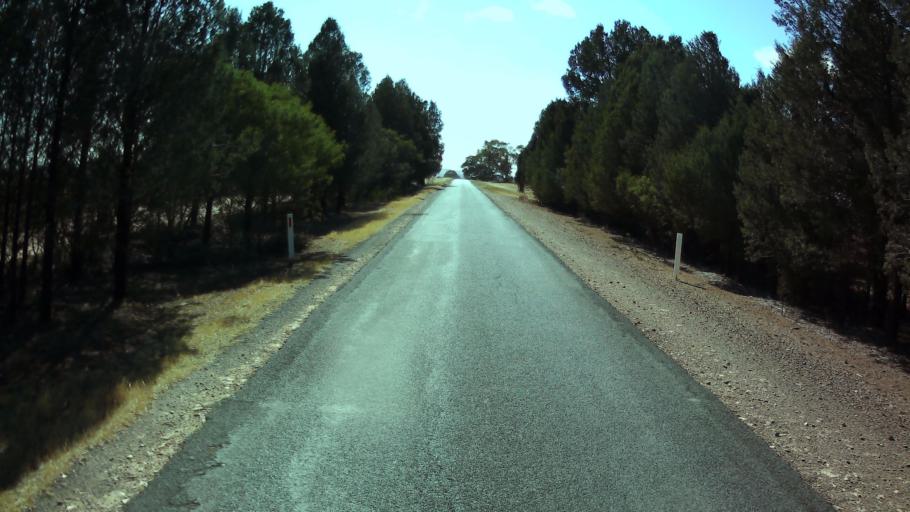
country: AU
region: New South Wales
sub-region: Weddin
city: Grenfell
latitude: -34.0633
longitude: 148.2862
